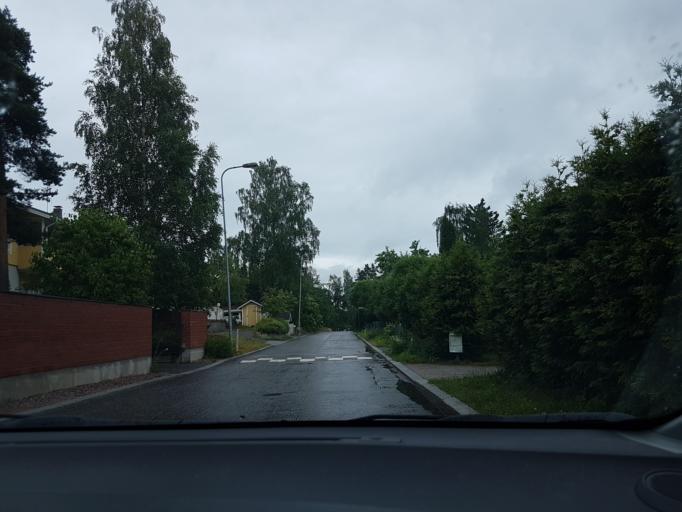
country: FI
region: Uusimaa
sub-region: Helsinki
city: Vantaa
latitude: 60.2310
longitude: 25.0944
